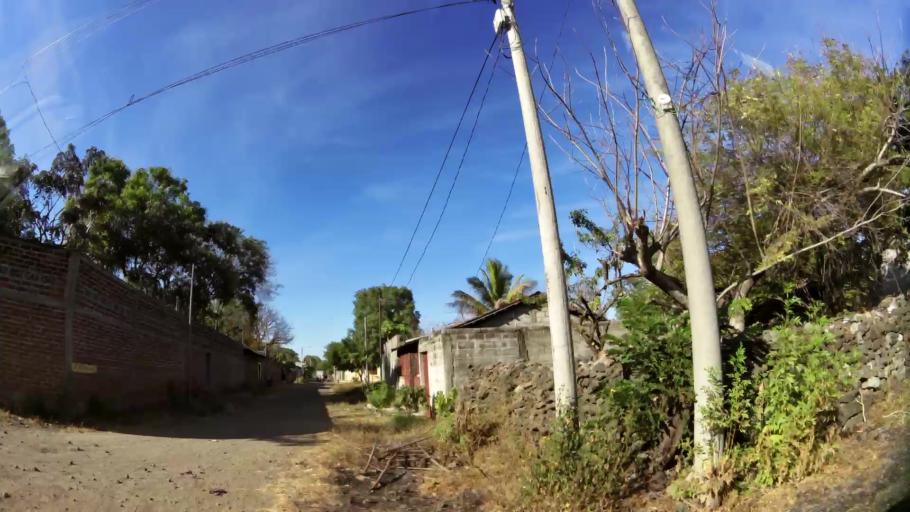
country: SV
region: San Miguel
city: San Miguel
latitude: 13.4660
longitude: -88.1926
